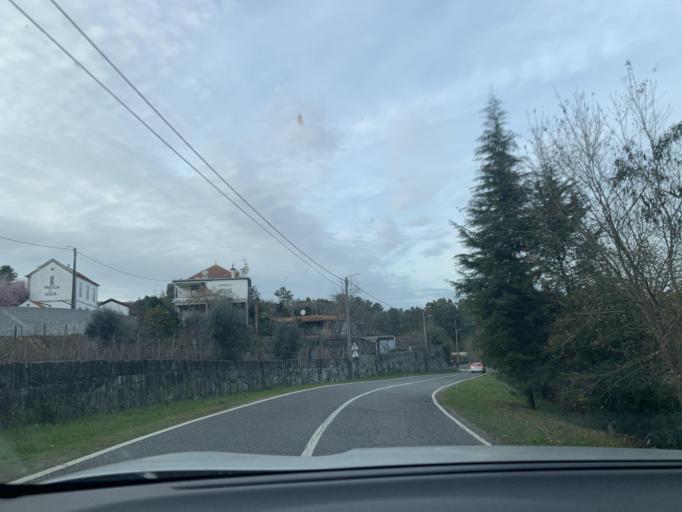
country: PT
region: Viseu
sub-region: Concelho de Tondela
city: Tondela
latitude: 40.5888
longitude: -8.0109
